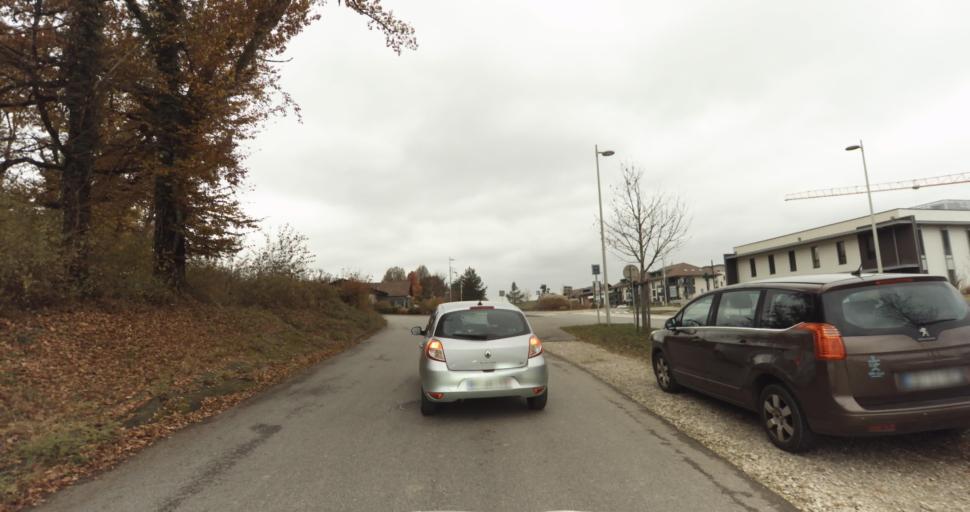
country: FR
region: Rhone-Alpes
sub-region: Departement de la Haute-Savoie
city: Chavanod
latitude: 45.8839
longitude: 6.0586
